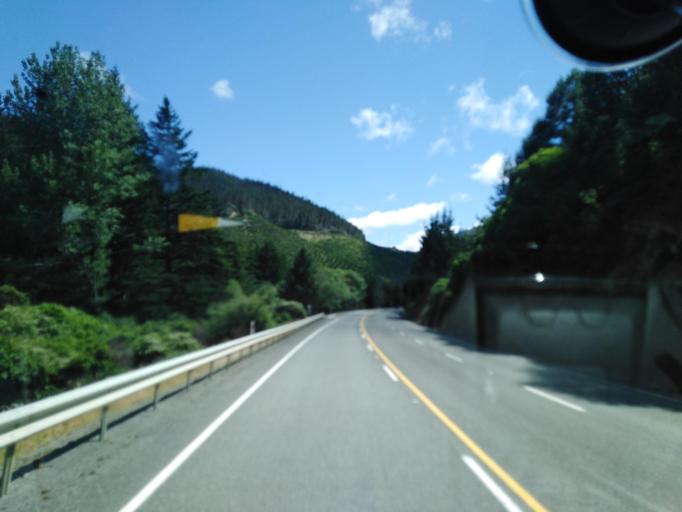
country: NZ
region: Nelson
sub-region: Nelson City
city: Nelson
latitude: -41.1819
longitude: 173.5596
